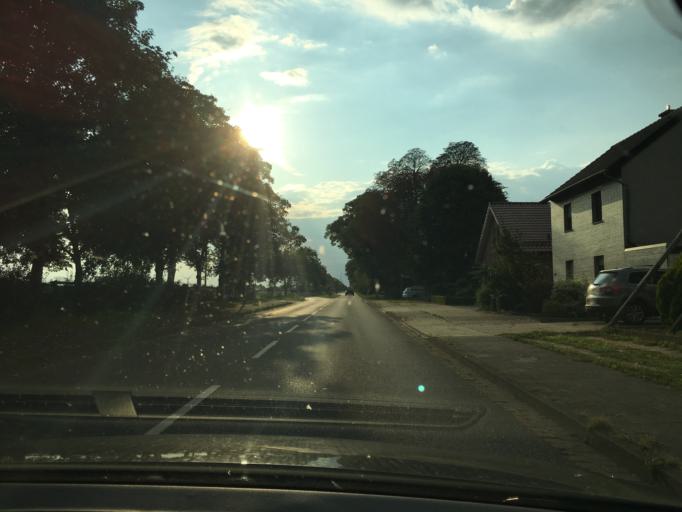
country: DE
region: North Rhine-Westphalia
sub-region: Regierungsbezirk Koln
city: Merzenich
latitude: 50.8115
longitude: 6.5783
